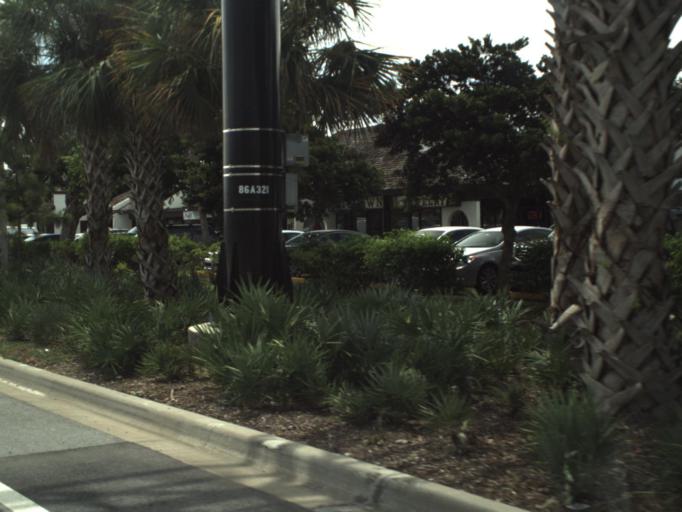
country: US
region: Florida
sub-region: Broward County
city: Pine Island Ridge
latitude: 26.1016
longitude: -80.2625
